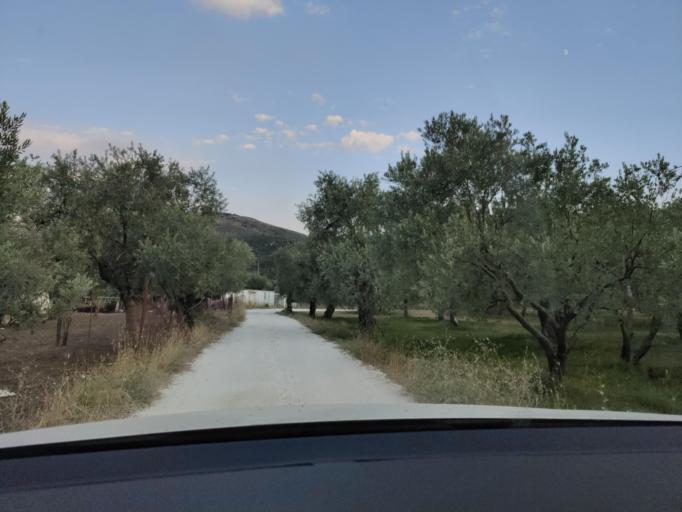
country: GR
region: East Macedonia and Thrace
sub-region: Nomos Kavalas
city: Prinos
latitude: 40.7498
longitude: 24.5739
